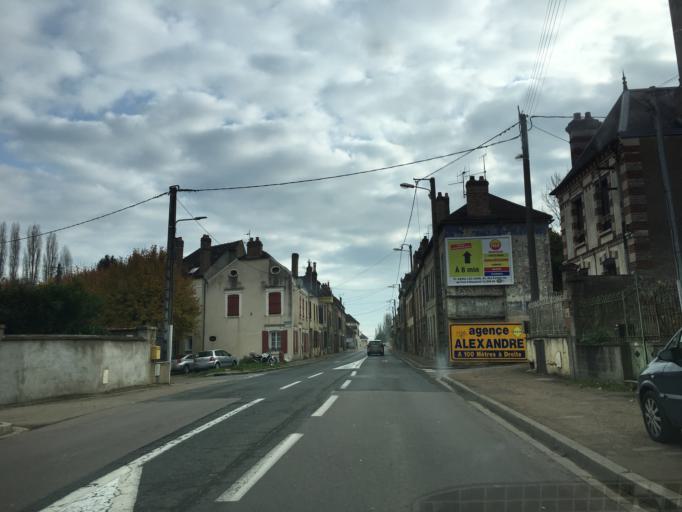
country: FR
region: Bourgogne
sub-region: Departement de l'Yonne
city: Pont-sur-Yonne
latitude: 48.2897
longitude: 3.2026
